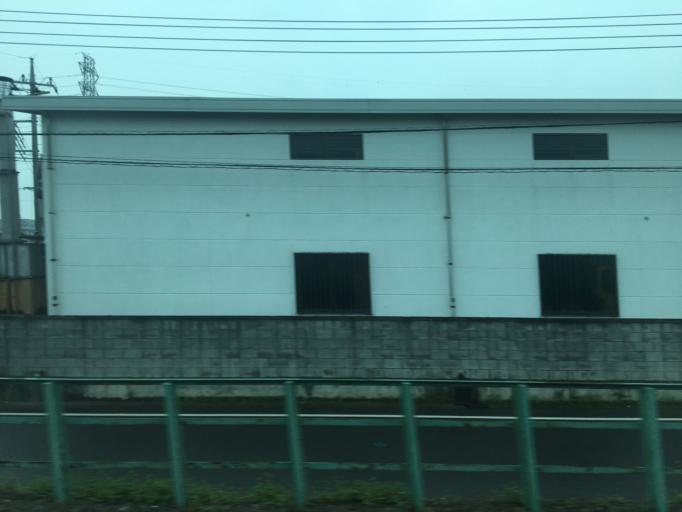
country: JP
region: Tochigi
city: Oyama
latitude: 36.2700
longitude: 139.7715
